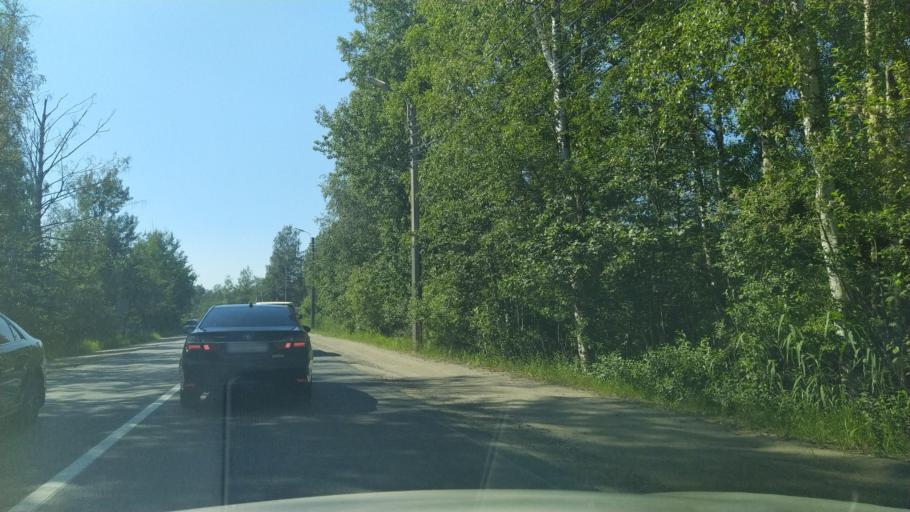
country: RU
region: St.-Petersburg
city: Beloostrov
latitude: 60.1413
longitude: 30.0259
